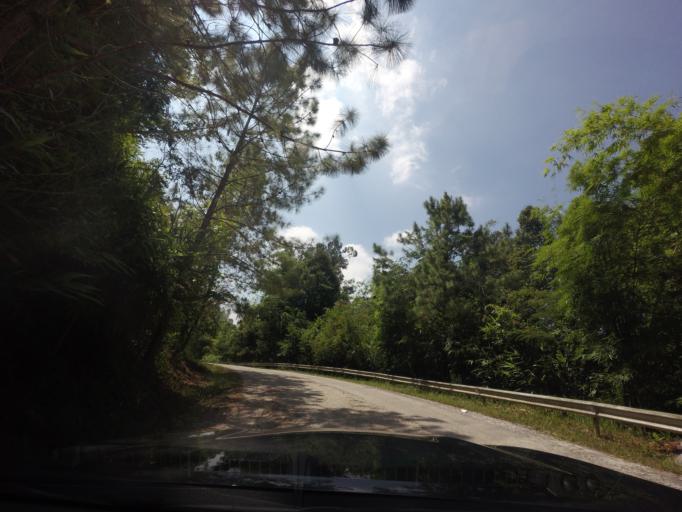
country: TH
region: Loei
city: Na Haeo
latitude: 17.5306
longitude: 100.9372
